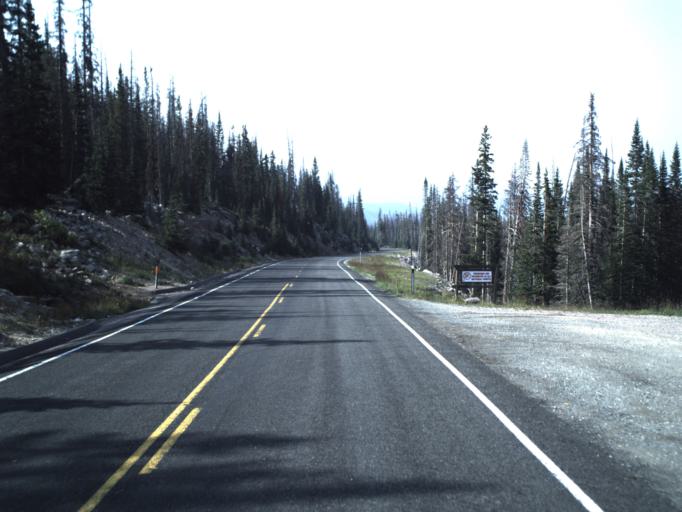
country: US
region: Utah
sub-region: Summit County
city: Kamas
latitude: 40.7357
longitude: -110.8676
